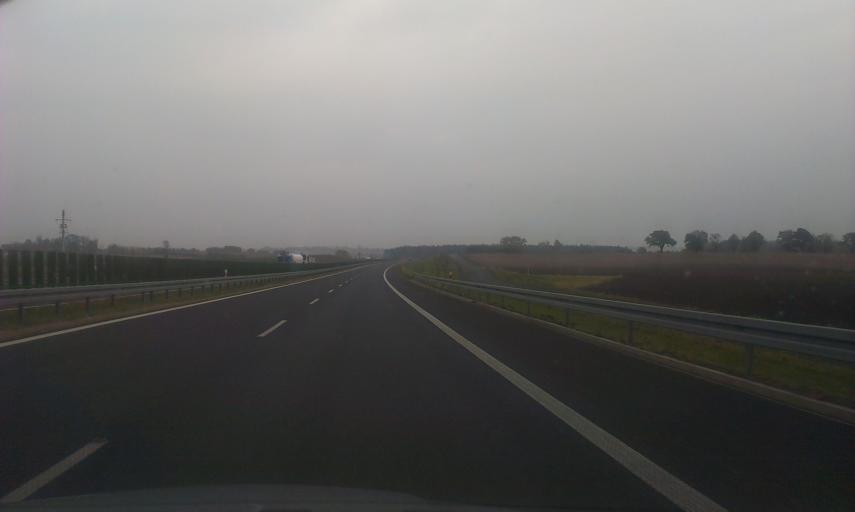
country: PL
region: Greater Poland Voivodeship
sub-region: Powiat poznanski
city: Rokietnica
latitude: 52.5052
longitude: 16.7717
